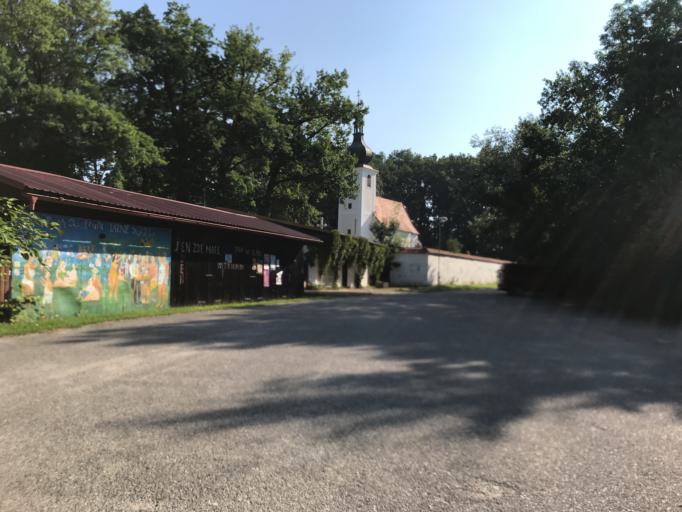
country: CZ
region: Jihocesky
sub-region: Okres Jindrichuv Hradec
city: Trebon
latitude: 48.9941
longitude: 14.7586
